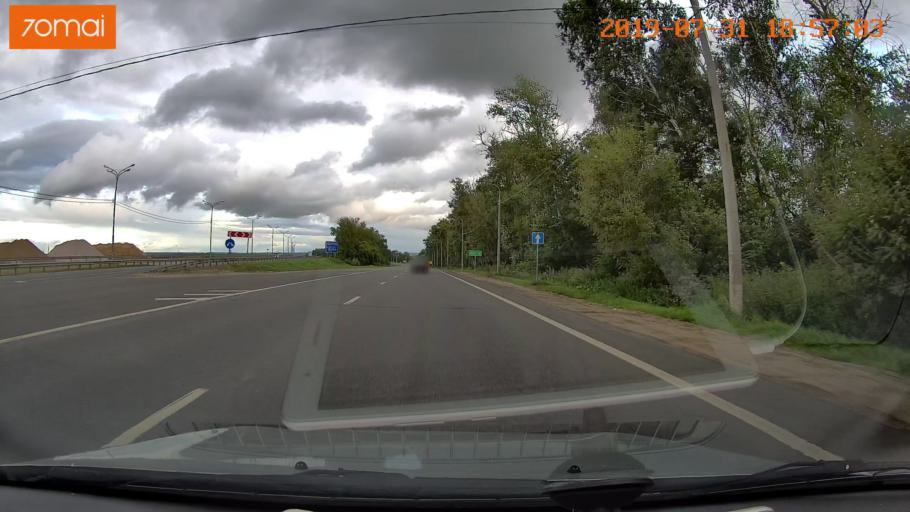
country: RU
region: Moskovskaya
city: Raduzhnyy
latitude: 55.1573
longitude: 38.6869
